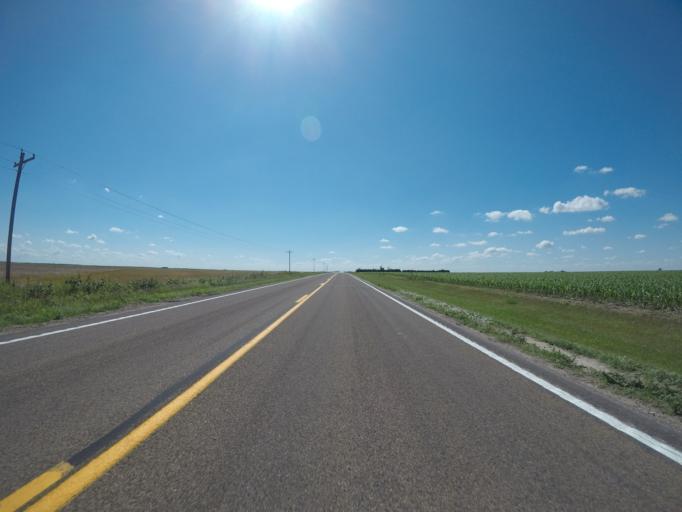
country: US
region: Nebraska
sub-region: Chase County
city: Imperial
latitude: 40.5376
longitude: -101.7528
